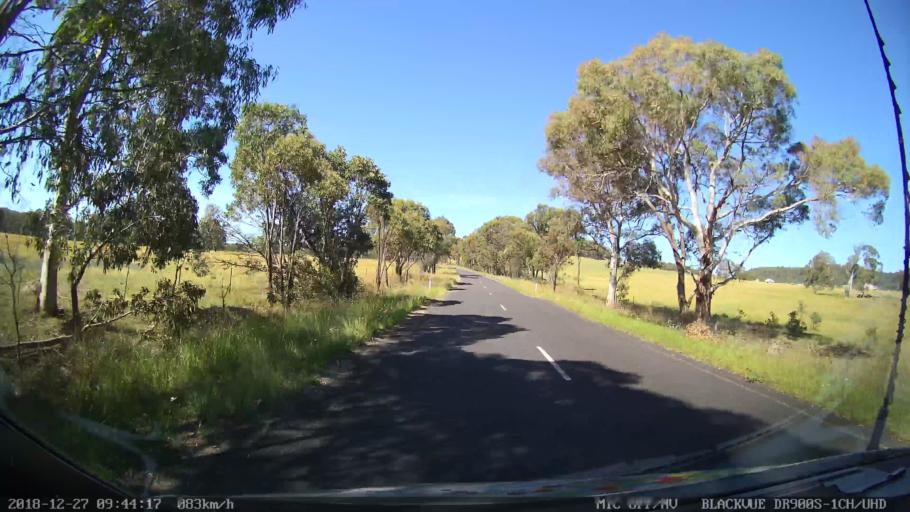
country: AU
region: New South Wales
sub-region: Lithgow
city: Portland
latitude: -33.3138
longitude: 149.9936
